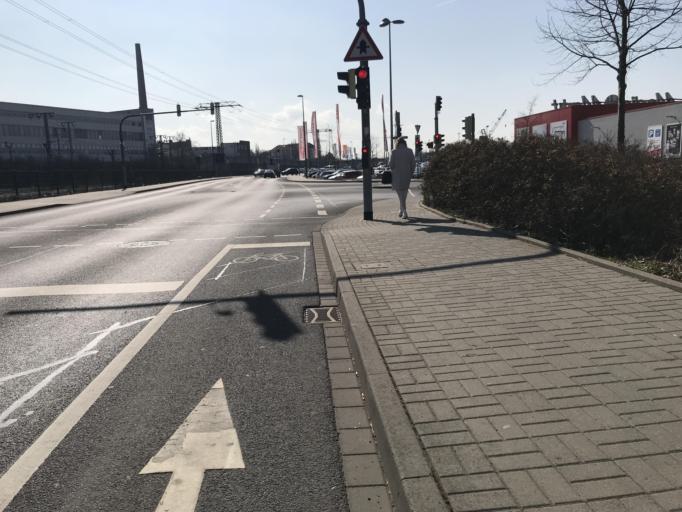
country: DE
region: Hesse
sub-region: Regierungsbezirk Kassel
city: Fulda
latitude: 50.5500
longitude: 9.6888
